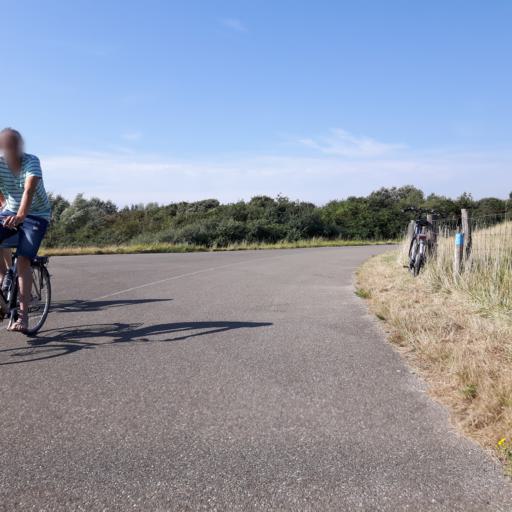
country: NL
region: Zeeland
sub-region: Gemeente Middelburg
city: Middelburg
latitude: 51.4512
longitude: 3.6538
